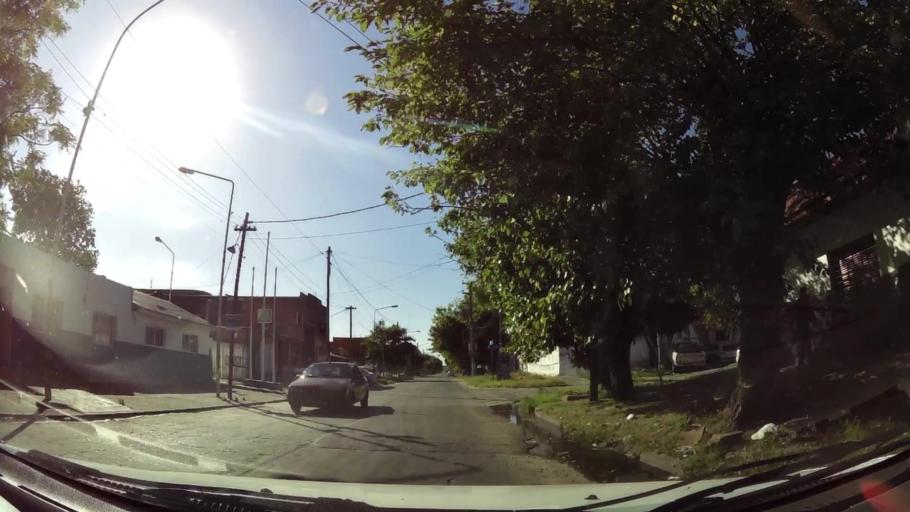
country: AR
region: Buenos Aires
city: Hurlingham
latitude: -34.5614
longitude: -58.6156
